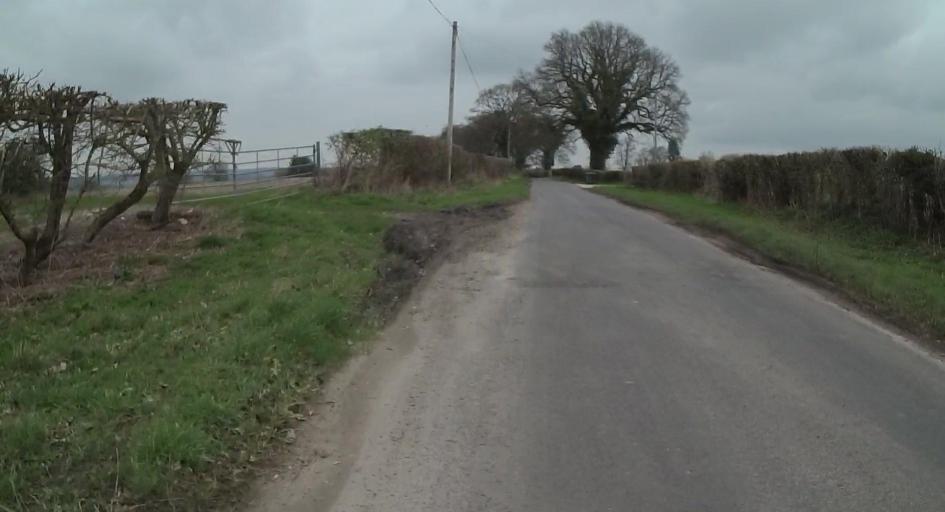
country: GB
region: England
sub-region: Hampshire
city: Kingsley
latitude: 51.1461
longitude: -0.9204
